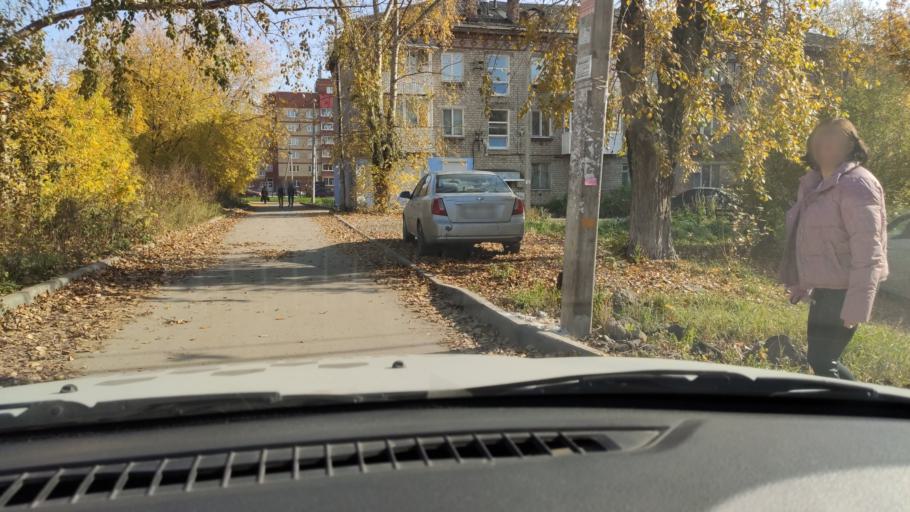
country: RU
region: Perm
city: Perm
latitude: 58.0357
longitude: 56.3569
